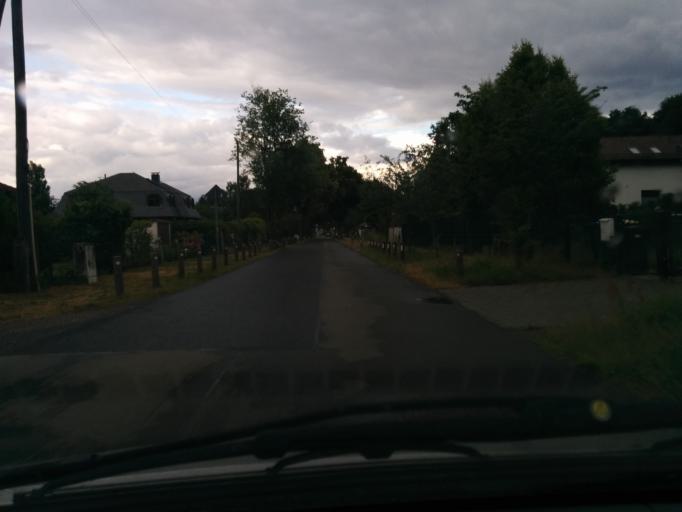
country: DE
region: Berlin
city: Staaken
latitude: 52.5653
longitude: 13.1406
